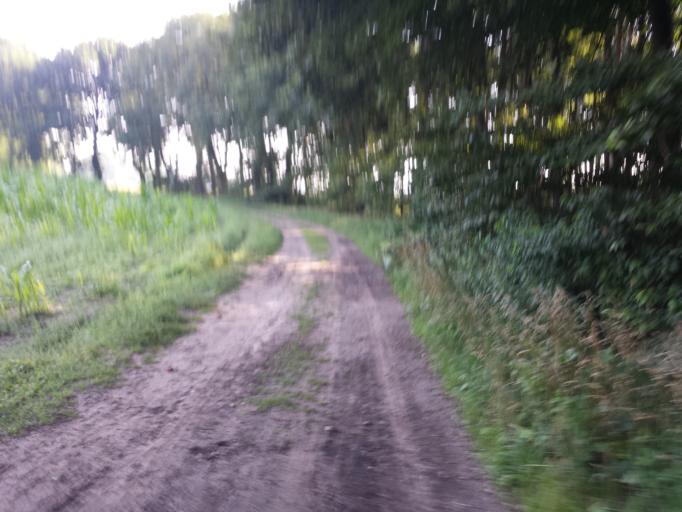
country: DE
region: North Rhine-Westphalia
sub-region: Regierungsbezirk Detmold
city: Guetersloh
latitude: 51.8915
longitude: 8.3333
